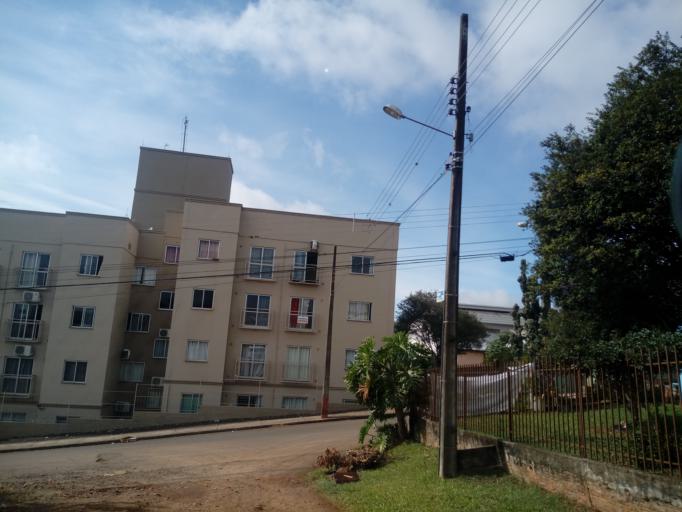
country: BR
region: Santa Catarina
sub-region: Chapeco
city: Chapeco
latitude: -27.1178
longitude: -52.6211
